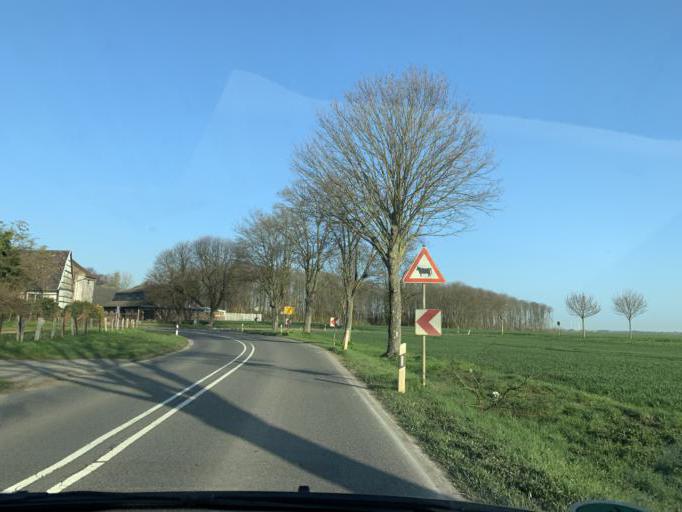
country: DE
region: North Rhine-Westphalia
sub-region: Regierungsbezirk Koln
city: Titz
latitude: 50.9675
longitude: 6.4618
